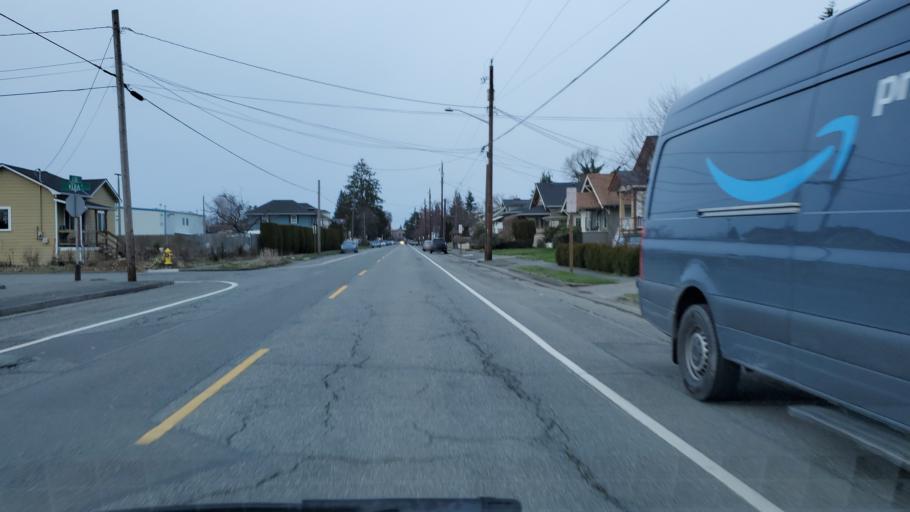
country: US
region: Washington
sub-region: Skagit County
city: Mount Vernon
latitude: 48.4102
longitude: -122.3368
